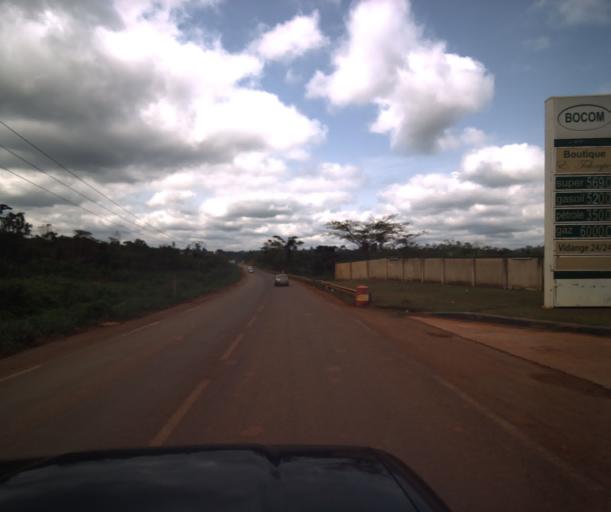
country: CM
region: Centre
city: Yaounde
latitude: 3.7929
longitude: 11.4740
